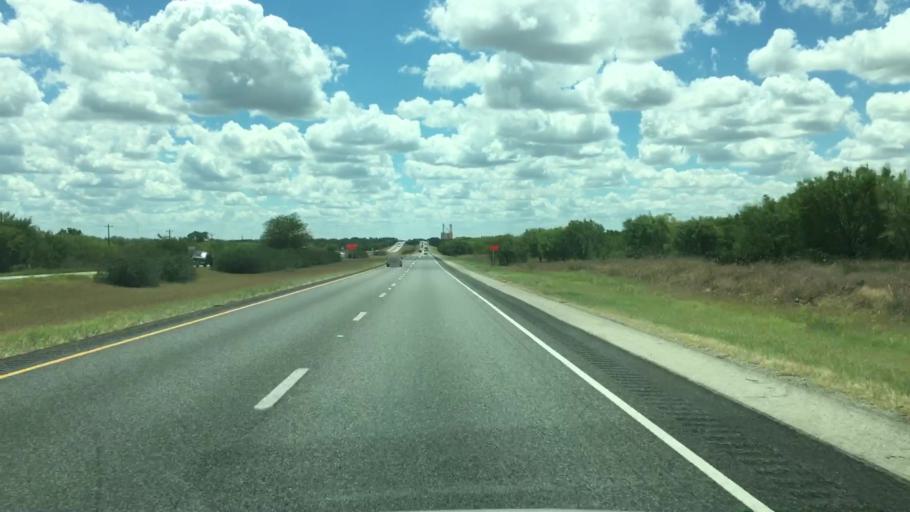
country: US
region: Texas
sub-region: Atascosa County
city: Pleasanton
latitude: 28.9734
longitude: -98.4350
